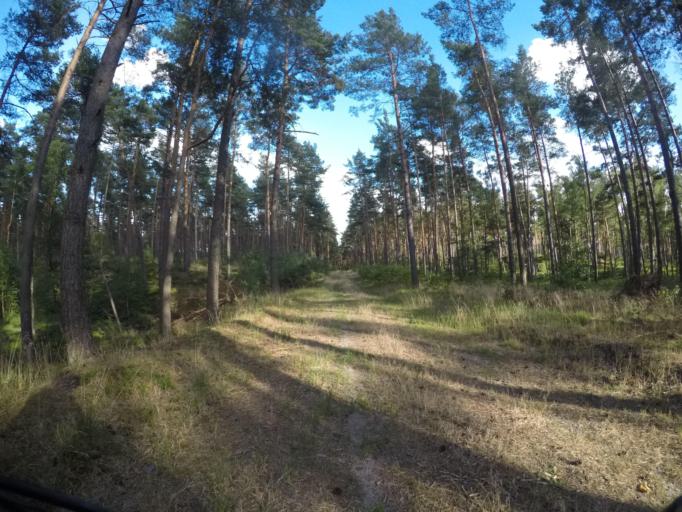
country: DE
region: Mecklenburg-Vorpommern
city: Lubtheen
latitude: 53.2488
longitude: 11.0072
